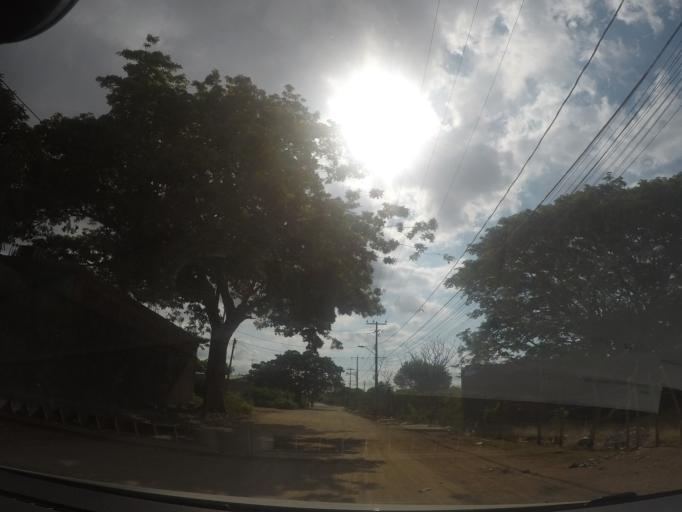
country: MX
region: Oaxaca
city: Juchitan de Zaragoza
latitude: 16.4294
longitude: -95.0328
